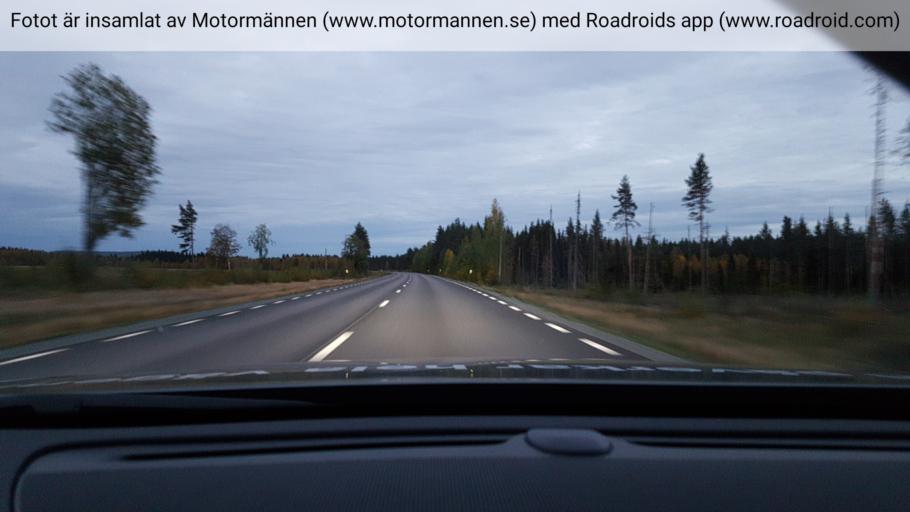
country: SE
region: Norrbotten
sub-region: Alvsbyns Kommun
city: AElvsbyn
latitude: 65.7621
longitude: 20.8768
